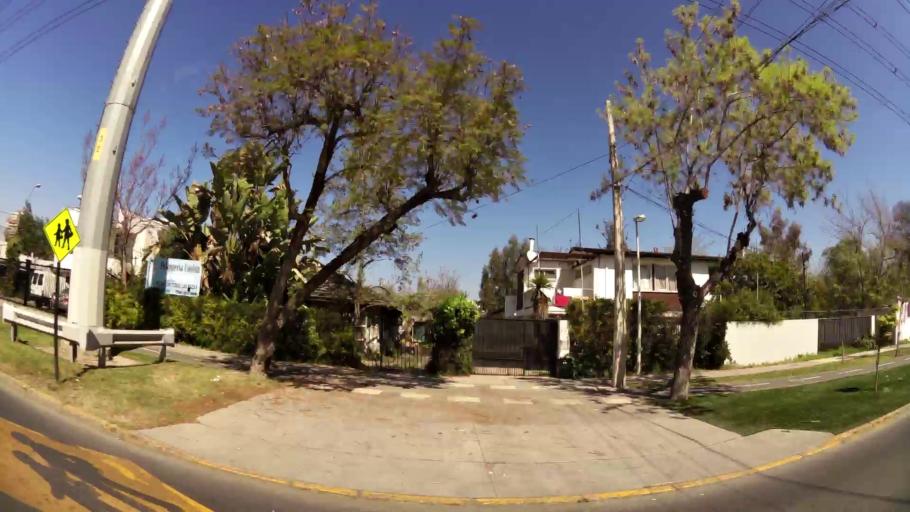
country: CL
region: Santiago Metropolitan
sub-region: Provincia de Santiago
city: Villa Presidente Frei, Nunoa, Santiago, Chile
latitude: -33.4118
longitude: -70.5613
